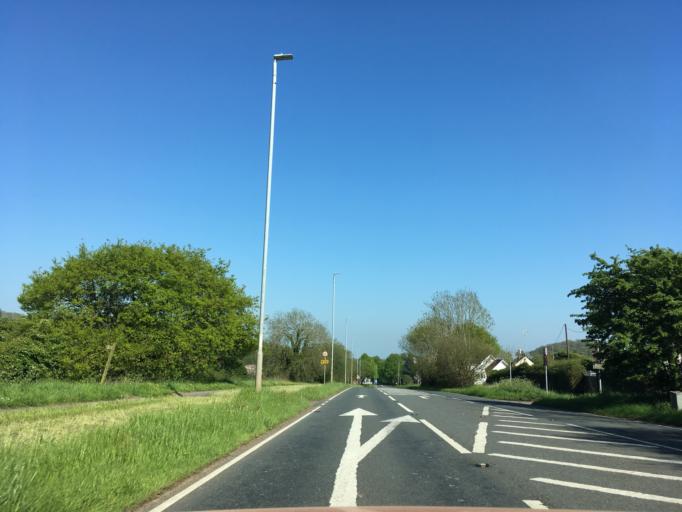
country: GB
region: Wales
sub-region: Newport
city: Llanvaches
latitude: 51.6169
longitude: -2.8493
